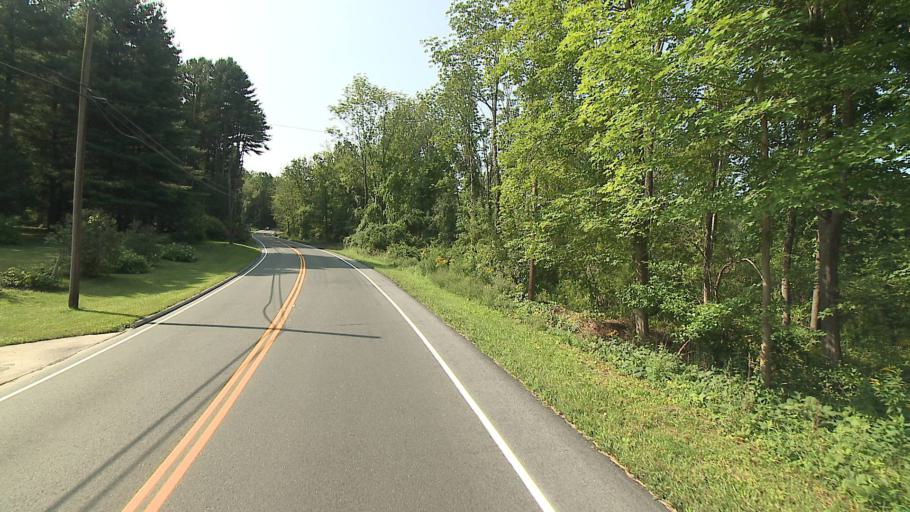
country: US
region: Connecticut
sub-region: Litchfield County
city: Kent
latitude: 41.6854
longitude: -73.5063
